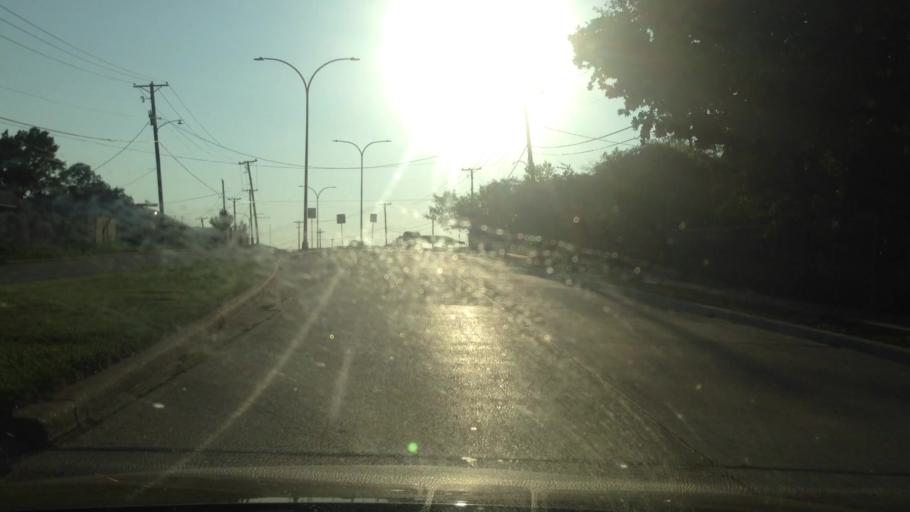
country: US
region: Texas
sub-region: Tarrant County
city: Dalworthington Gardens
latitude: 32.6825
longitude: -97.1881
